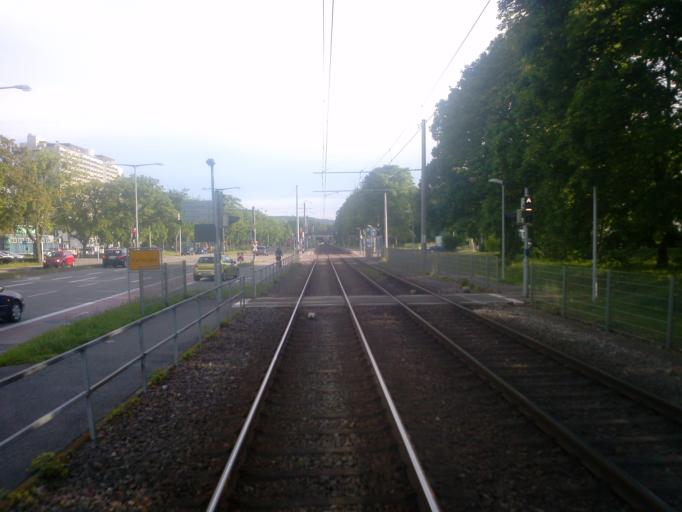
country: DE
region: Baden-Wuerttemberg
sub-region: Karlsruhe Region
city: Karlsruhe
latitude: 48.9854
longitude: 8.4035
